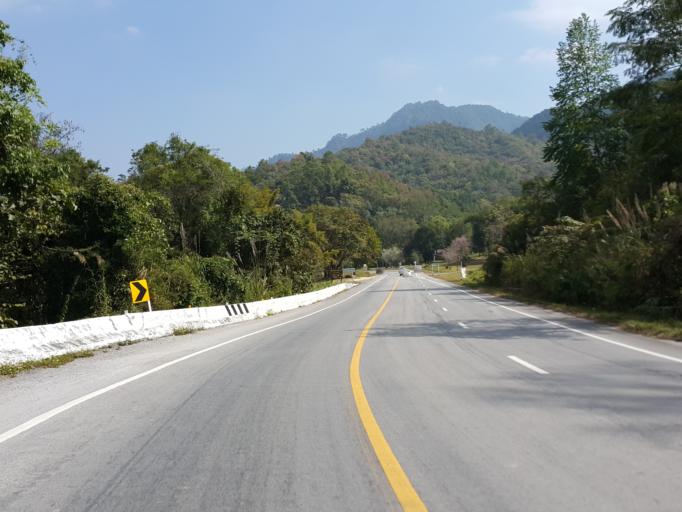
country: TH
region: Lampang
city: Wang Nuea
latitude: 19.0785
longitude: 99.3964
